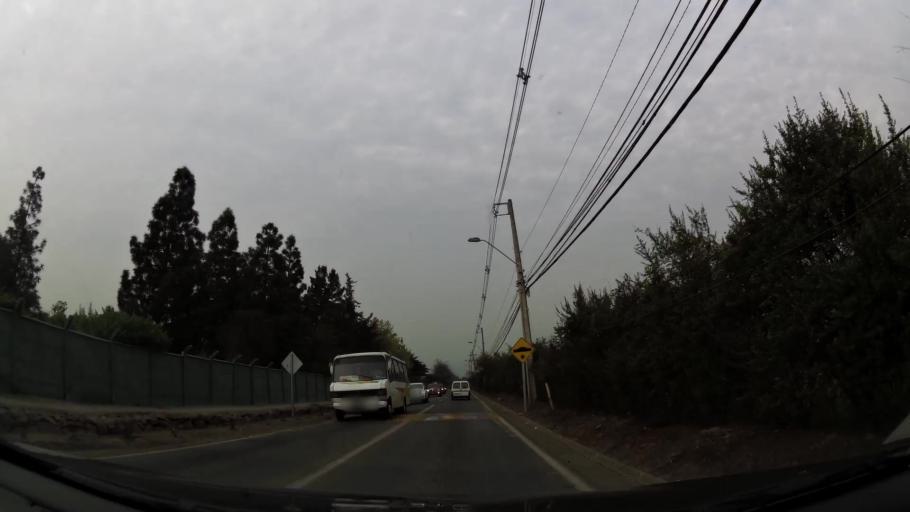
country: CL
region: Santiago Metropolitan
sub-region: Provincia de Chacabuco
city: Chicureo Abajo
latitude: -33.2863
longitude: -70.6602
